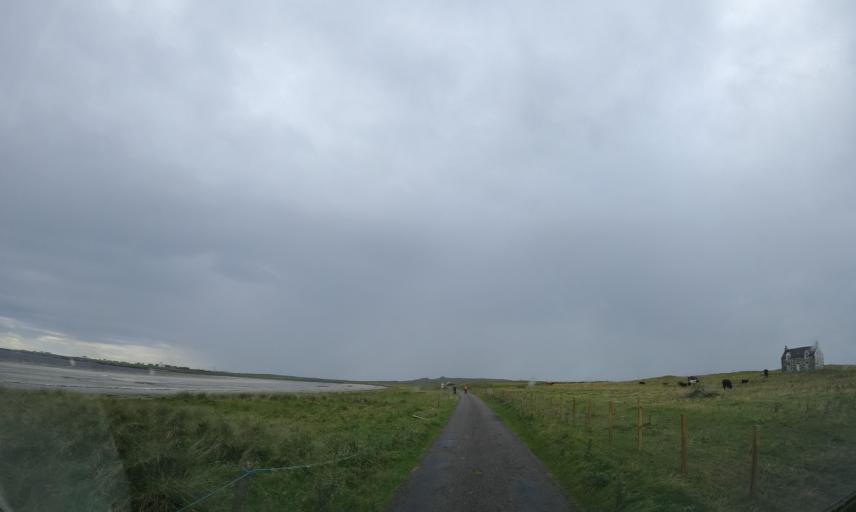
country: GB
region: Scotland
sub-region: Eilean Siar
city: Barra
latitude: 56.5184
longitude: -6.8119
